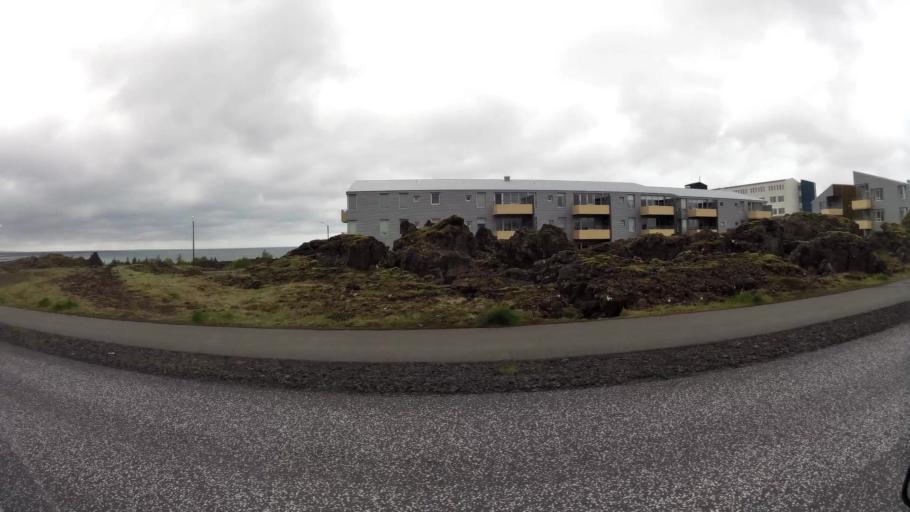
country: IS
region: Capital Region
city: Hafnarfjoerdur
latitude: 64.0788
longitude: -21.9721
